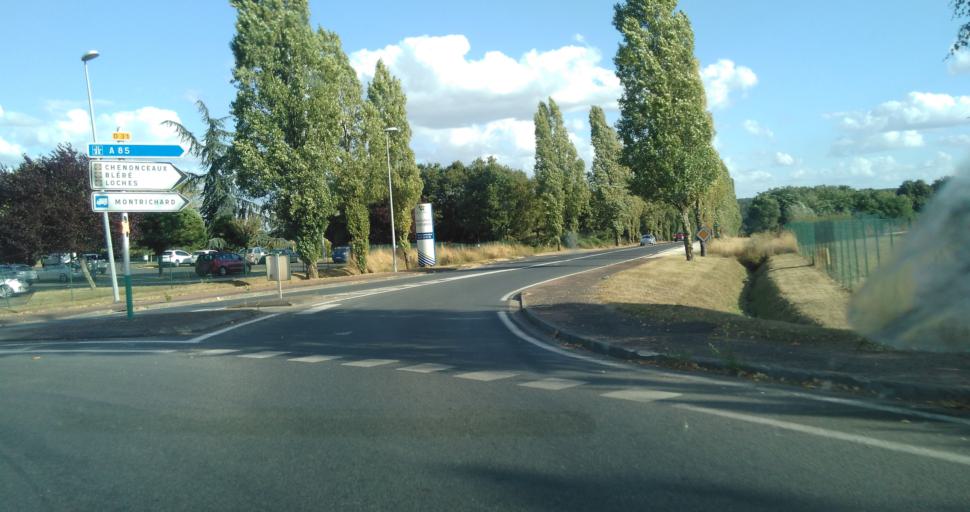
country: FR
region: Centre
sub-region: Departement d'Indre-et-Loire
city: Charge
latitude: 47.4144
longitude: 1.0175
